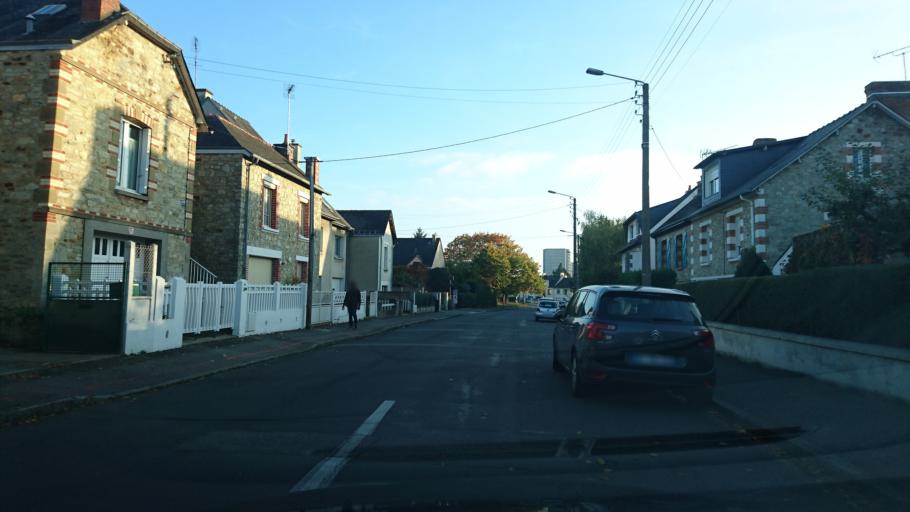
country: FR
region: Brittany
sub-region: Departement d'Ille-et-Vilaine
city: Rennes
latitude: 48.0930
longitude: -1.6618
